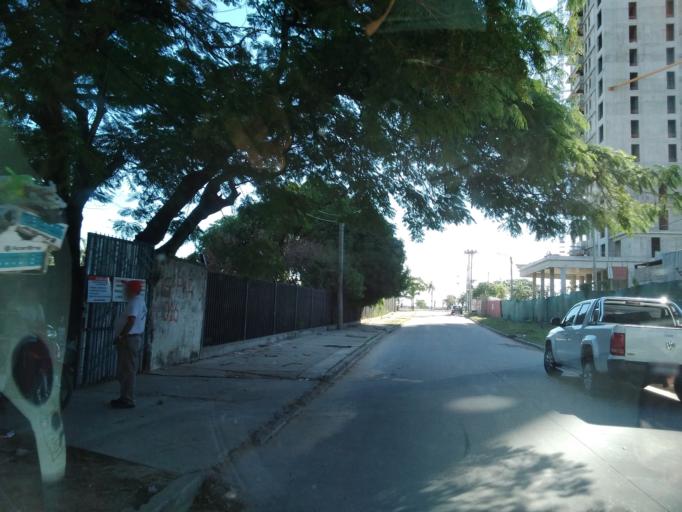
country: AR
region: Corrientes
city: Corrientes
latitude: -27.4760
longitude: -58.8546
